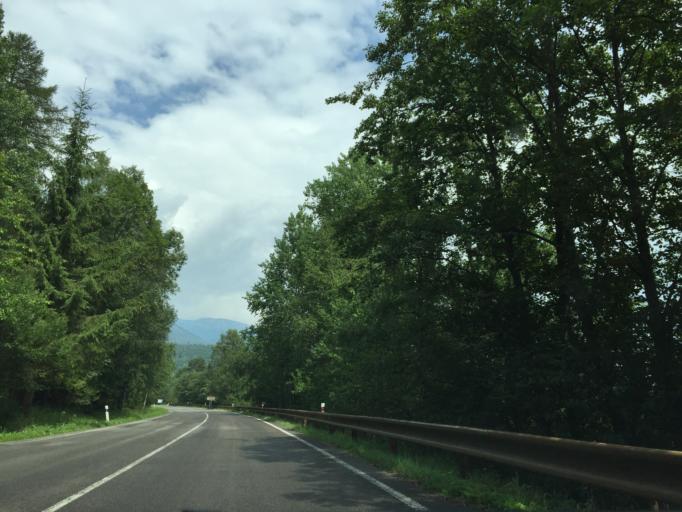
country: SK
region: Presovsky
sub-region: Okres Poprad
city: Nova Lesna
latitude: 49.1584
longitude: 20.2728
